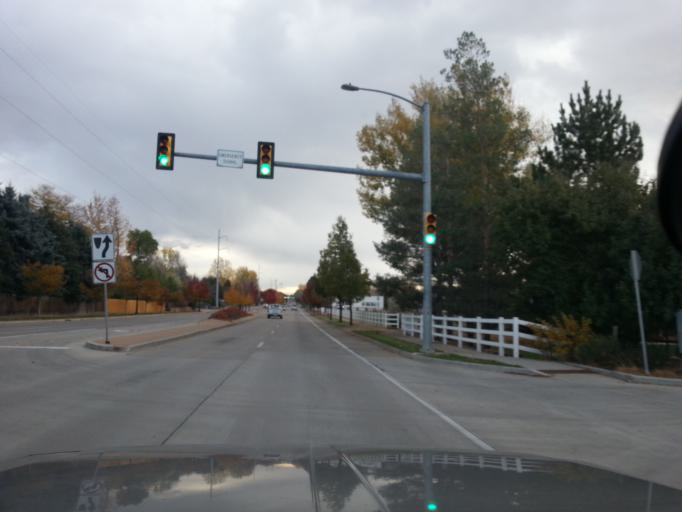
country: US
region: Colorado
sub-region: Larimer County
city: Fort Collins
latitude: 40.5528
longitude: -105.1131
